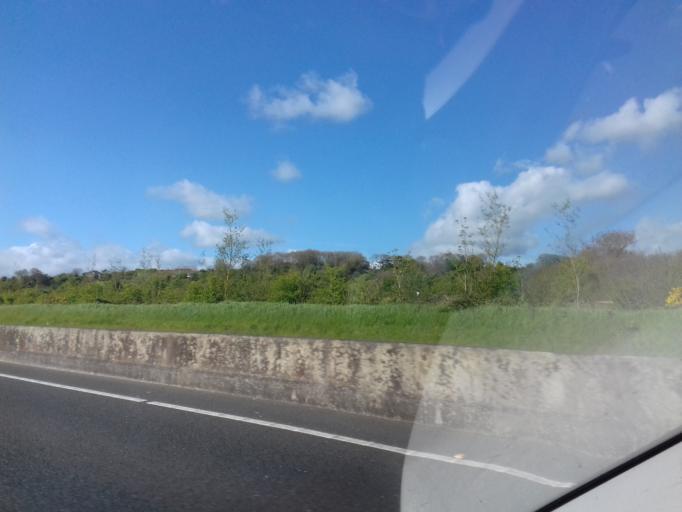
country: IE
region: Munster
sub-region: Waterford
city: Waterford
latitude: 52.3355
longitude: -7.1592
